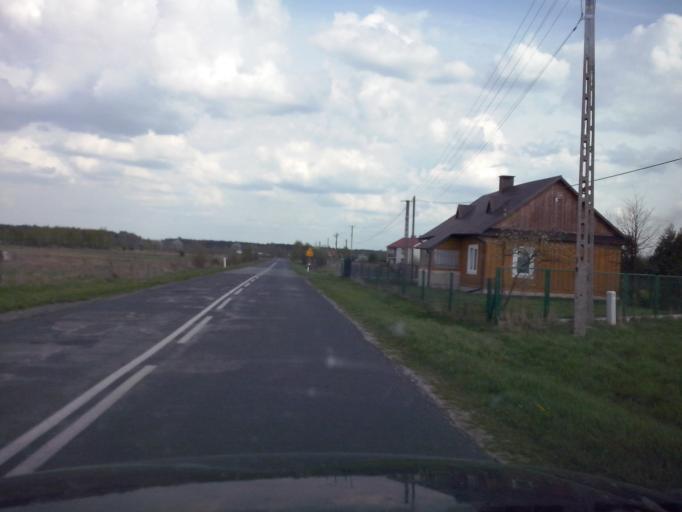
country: PL
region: Subcarpathian Voivodeship
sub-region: Powiat lezajski
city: Letownia
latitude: 50.3646
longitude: 22.2243
